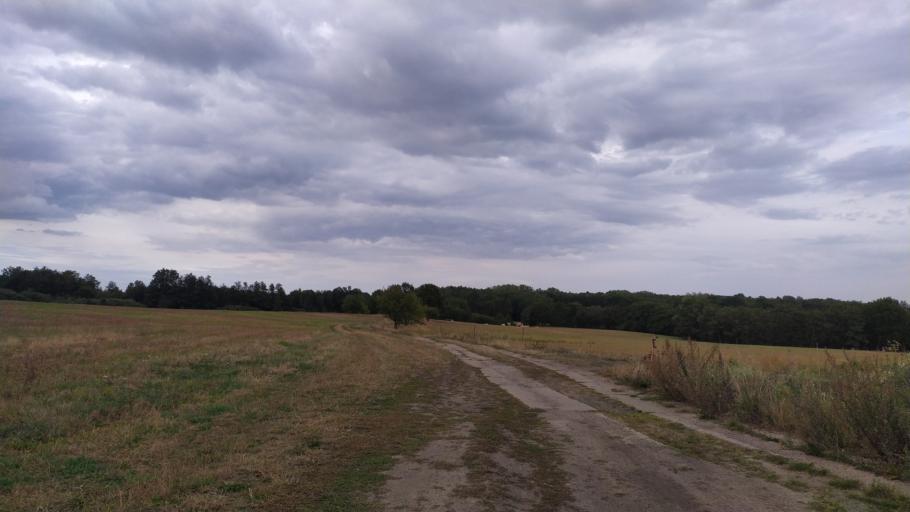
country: DE
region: Mecklenburg-Vorpommern
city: Wolgast
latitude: 54.0574
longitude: 13.8254
